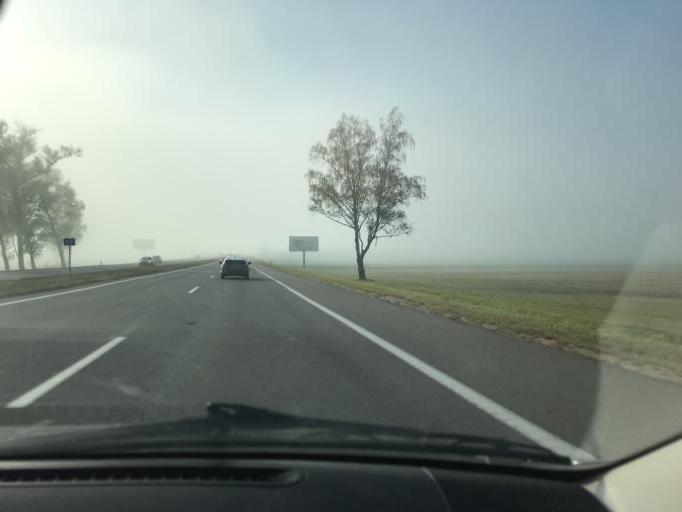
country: BY
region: Minsk
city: Yubilyeyny
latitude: 53.7814
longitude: 27.5253
